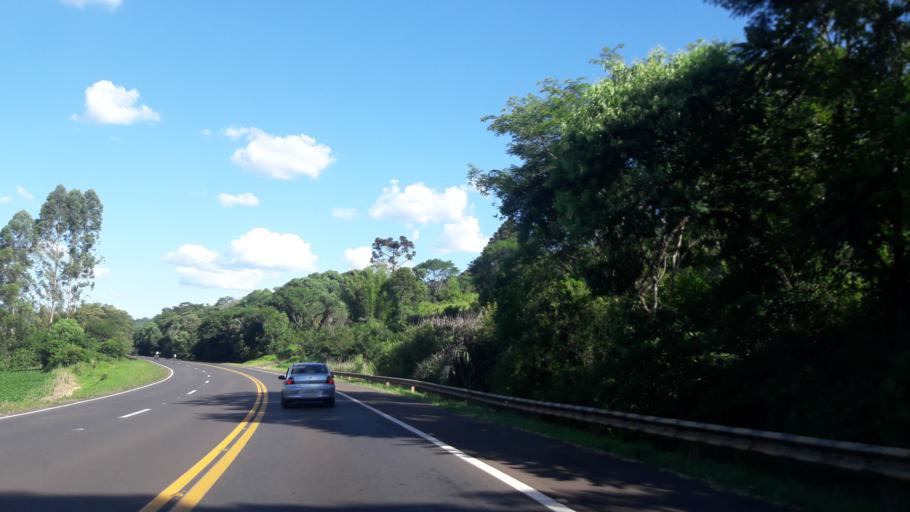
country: BR
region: Parana
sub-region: Laranjeiras Do Sul
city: Laranjeiras do Sul
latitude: -25.4147
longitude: -52.0780
